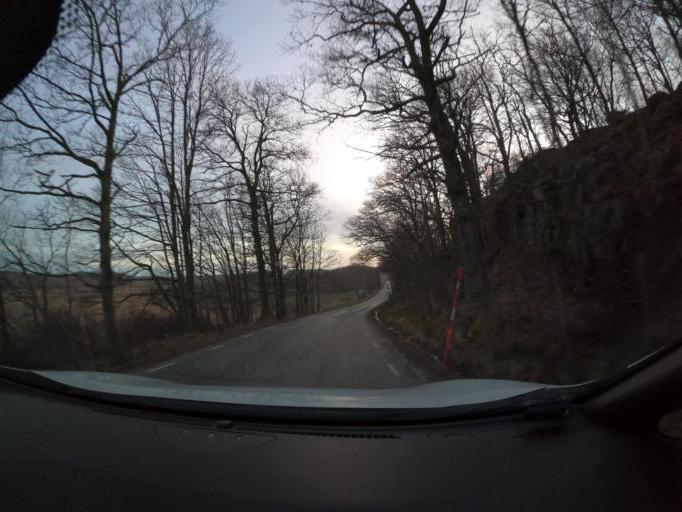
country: SE
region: Vaestra Goetaland
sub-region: Harryda Kommun
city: Molnlycke
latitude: 57.6079
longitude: 12.1515
